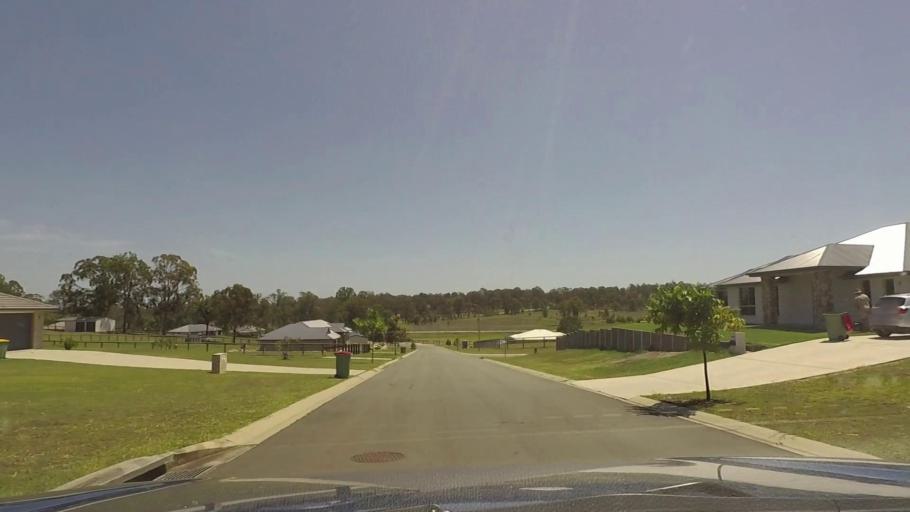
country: AU
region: Queensland
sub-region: Logan
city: Cedar Vale
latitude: -27.8888
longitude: 152.9830
